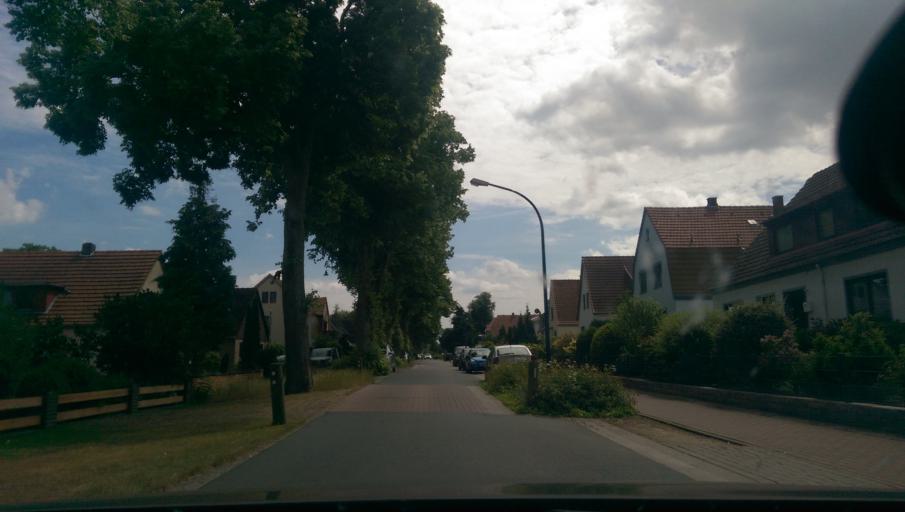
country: DE
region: Lower Saxony
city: Oyten
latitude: 53.0637
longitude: 9.0156
